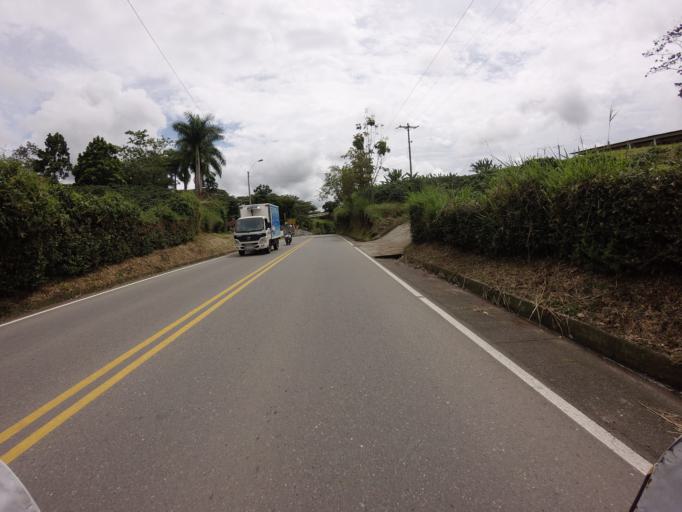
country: CO
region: Valle del Cauca
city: Alcala
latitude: 4.6628
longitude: -75.7774
